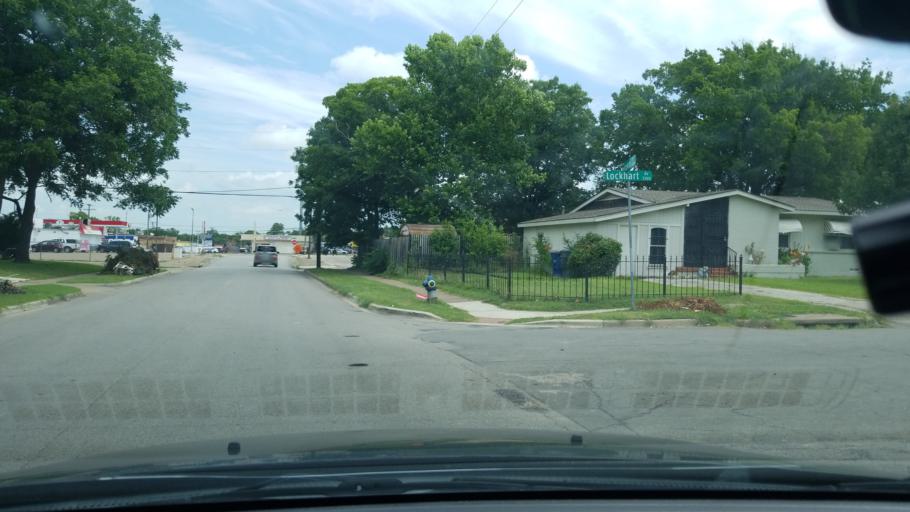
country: US
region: Texas
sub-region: Dallas County
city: Mesquite
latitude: 32.8200
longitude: -96.6777
